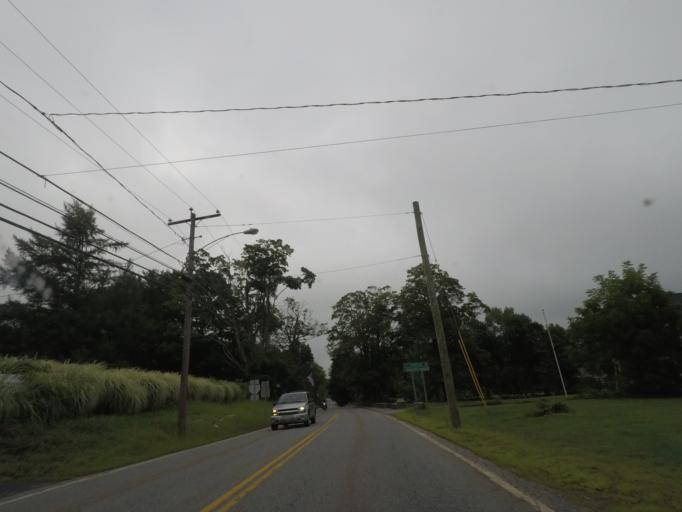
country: US
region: Connecticut
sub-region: Windham County
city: Thompson
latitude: 41.9598
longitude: -71.8616
